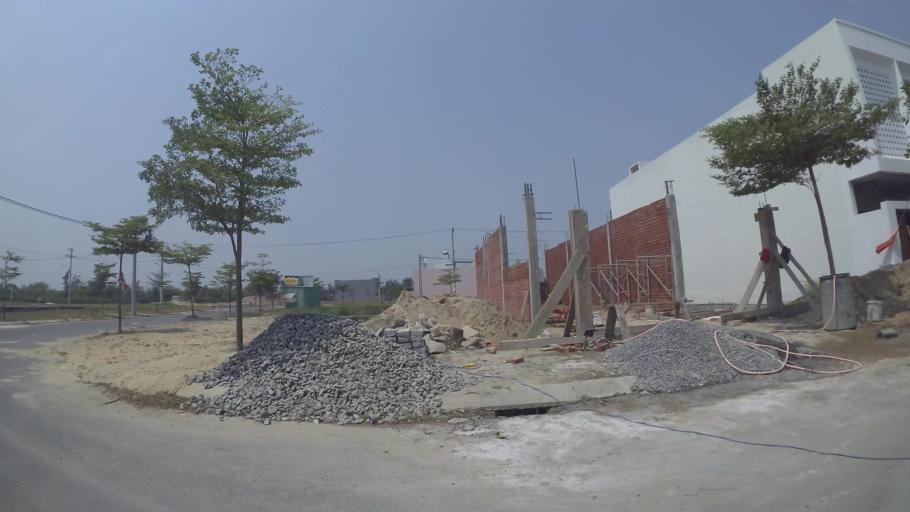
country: VN
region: Da Nang
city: Ngu Hanh Son
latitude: 15.9849
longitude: 108.2615
